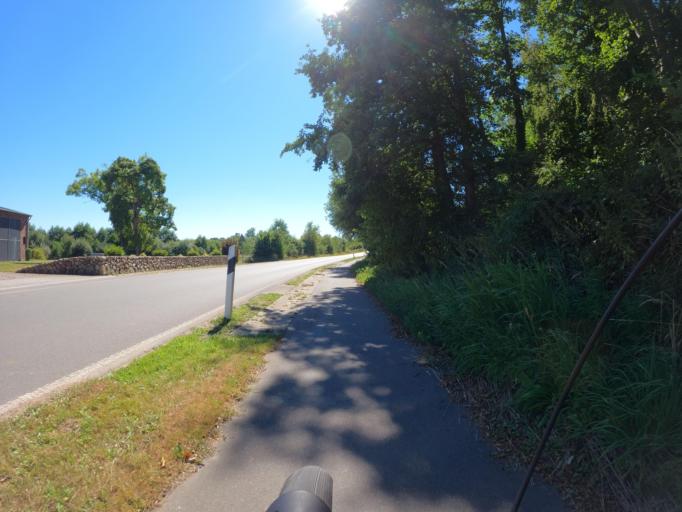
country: DE
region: Schleswig-Holstein
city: Dollerup
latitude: 54.7926
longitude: 9.7247
